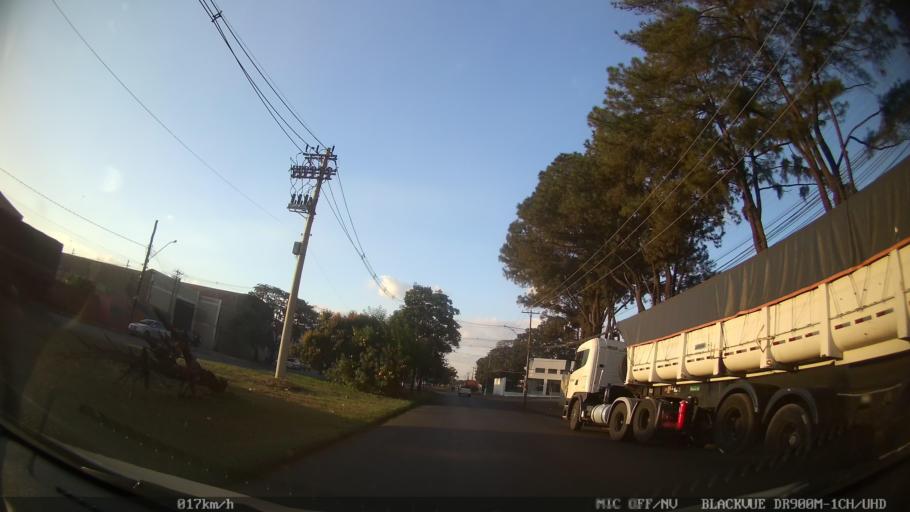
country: BR
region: Sao Paulo
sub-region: Ribeirao Preto
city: Ribeirao Preto
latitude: -21.1438
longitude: -47.7842
